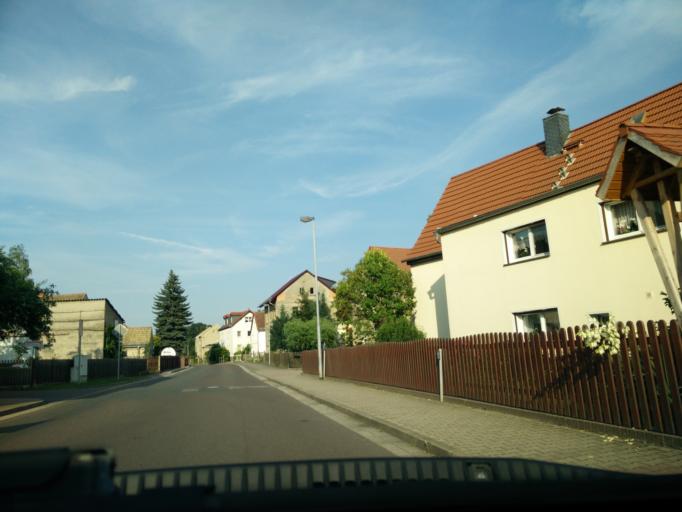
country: DE
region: Saxony
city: Frohburg
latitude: 51.0580
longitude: 12.5853
